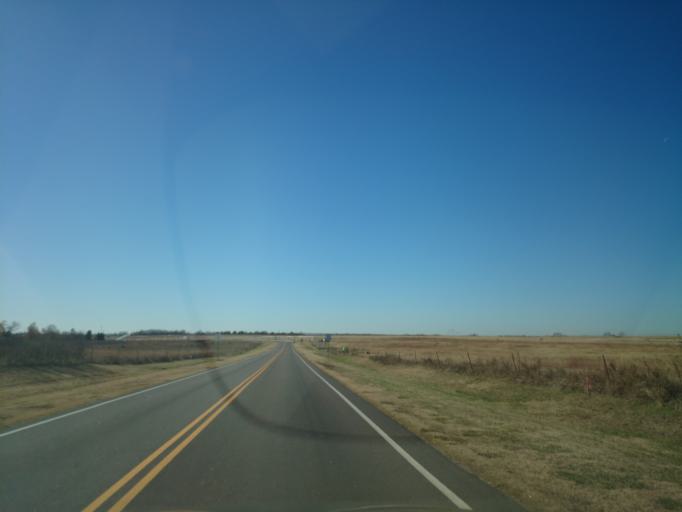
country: US
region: Oklahoma
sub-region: Payne County
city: Stillwater
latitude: 36.1528
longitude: -97.0827
